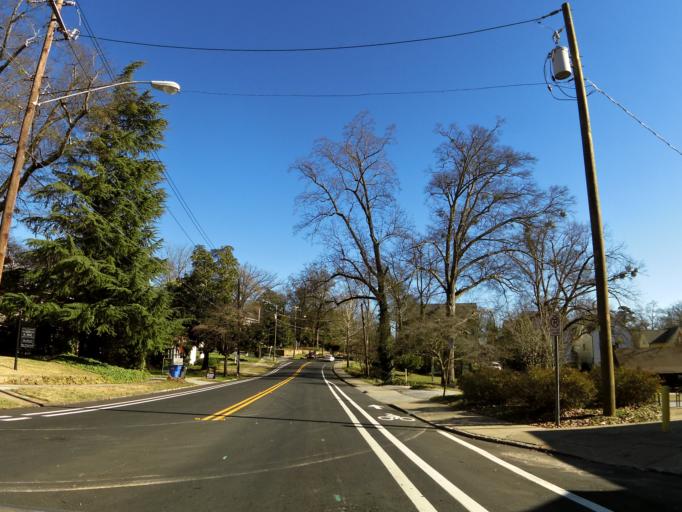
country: US
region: South Carolina
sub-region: Greenville County
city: Greenville
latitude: 34.8580
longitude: -82.3942
